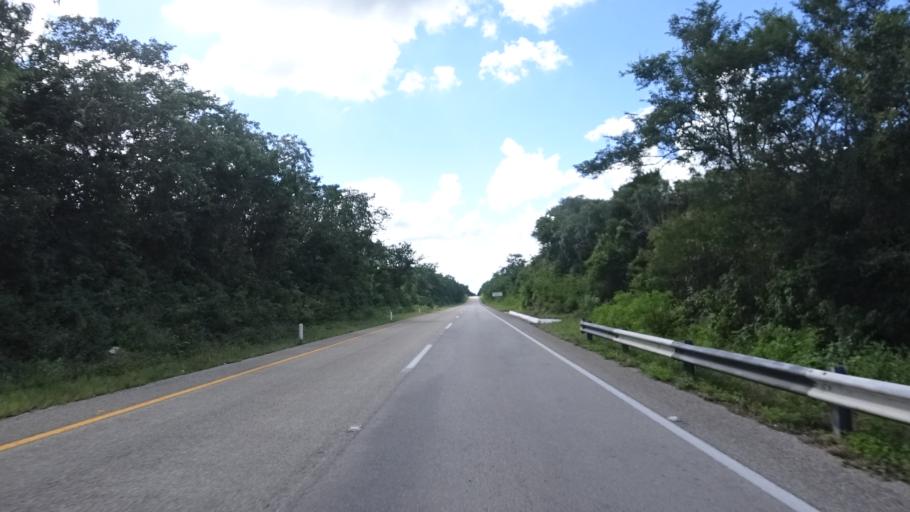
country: MX
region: Yucatan
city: Chichen-Itza
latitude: 20.7180
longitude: -88.5258
